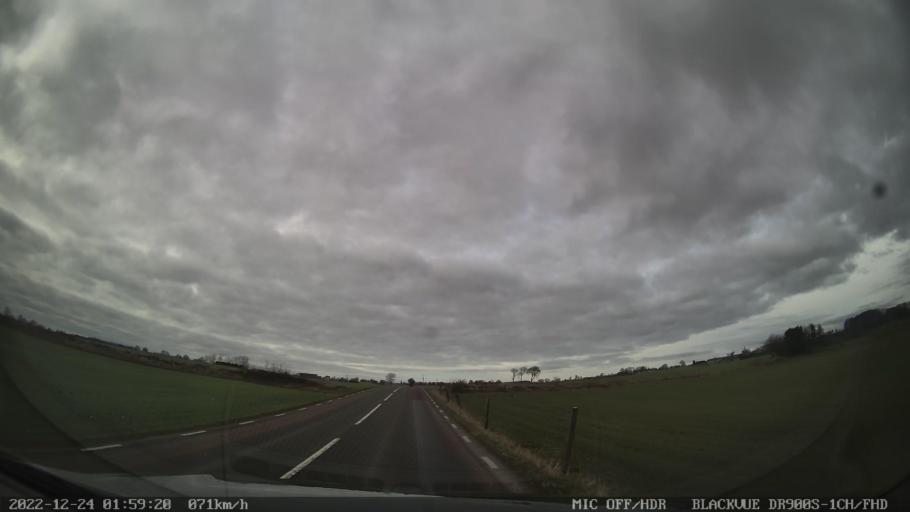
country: SE
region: Skane
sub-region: Tomelilla Kommun
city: Tomelilla
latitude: 55.6076
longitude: 14.0173
